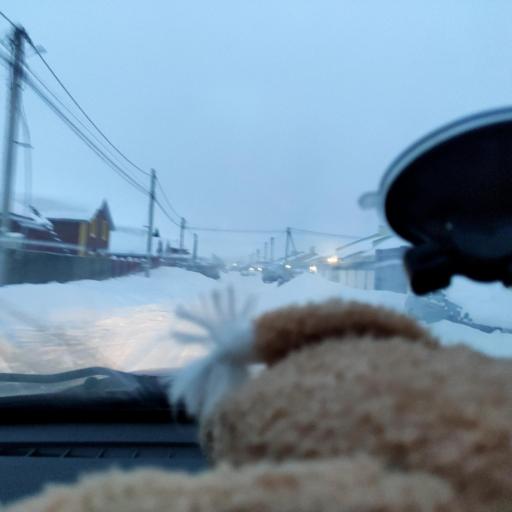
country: RU
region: Samara
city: Podstepki
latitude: 53.5091
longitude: 49.1736
